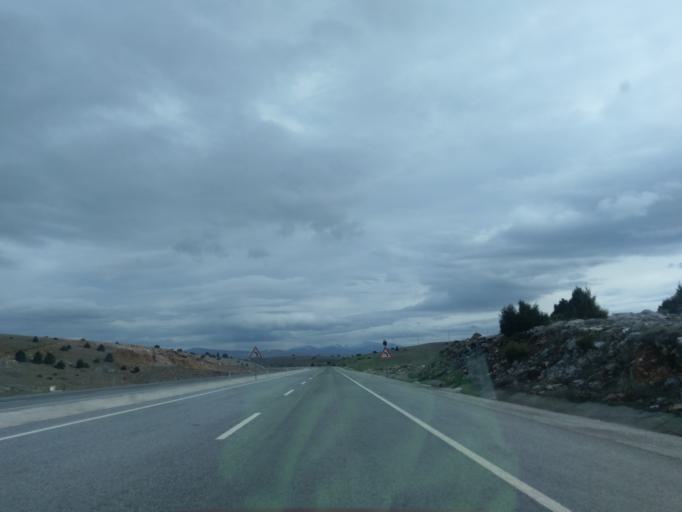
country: TR
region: Kuetahya
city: Aslanapa
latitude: 39.2337
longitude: 29.7815
